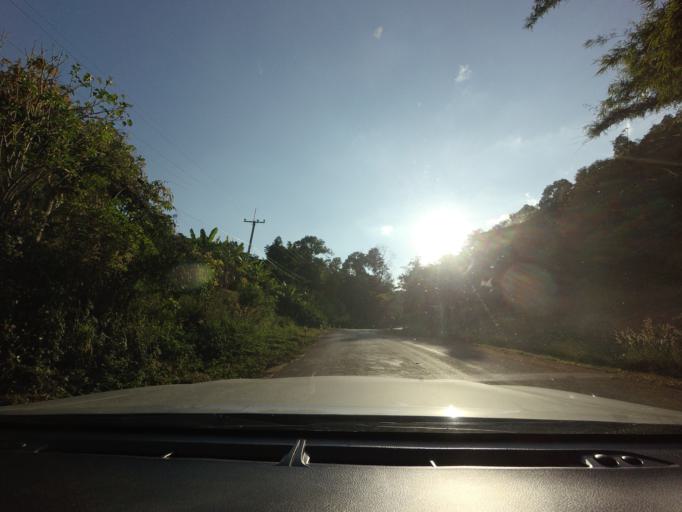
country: TH
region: Chiang Mai
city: Chai Prakan
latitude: 19.6192
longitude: 99.1649
